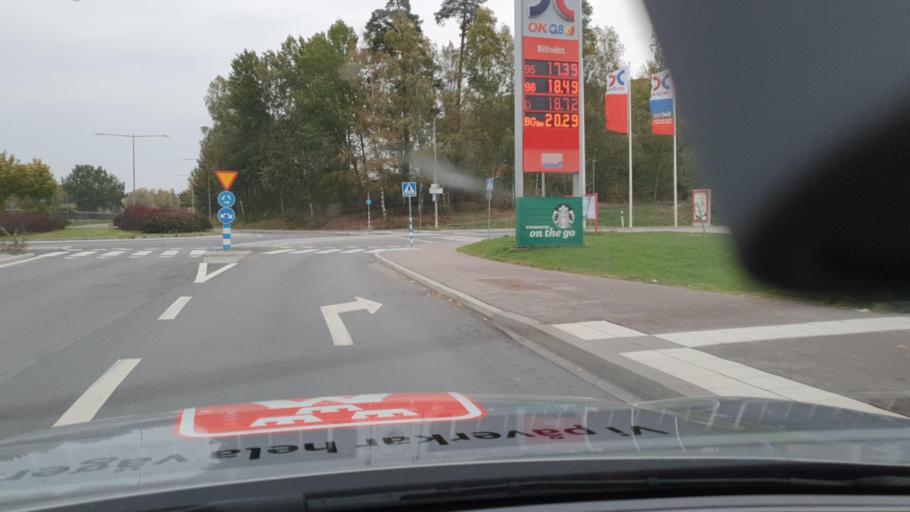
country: SE
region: Stockholm
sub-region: Sodertalje Kommun
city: Soedertaelje
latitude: 59.1787
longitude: 17.6145
